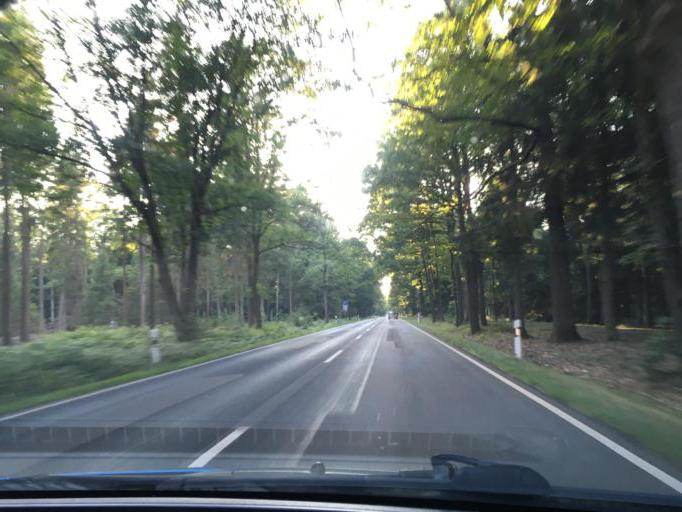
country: DE
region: Lower Saxony
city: Unterluss
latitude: 52.8059
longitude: 10.3677
